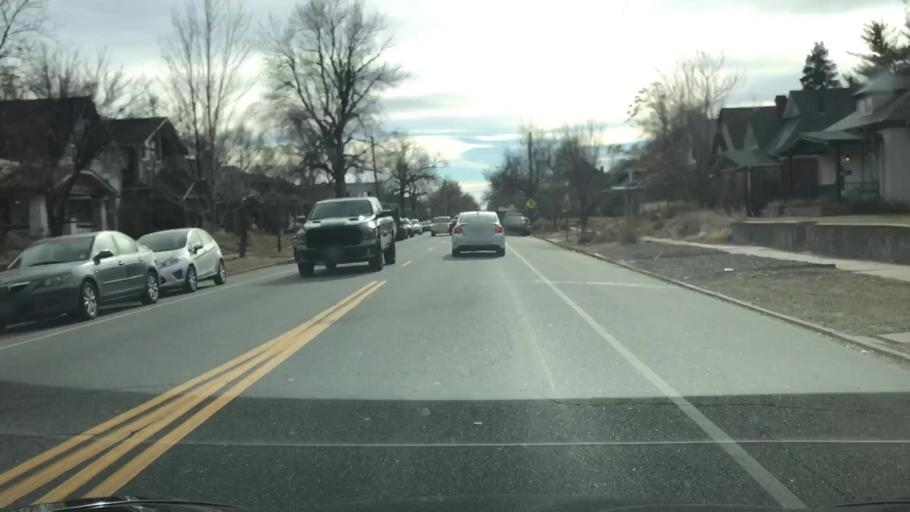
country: US
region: Colorado
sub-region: Denver County
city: Denver
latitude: 39.7070
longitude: -104.9828
